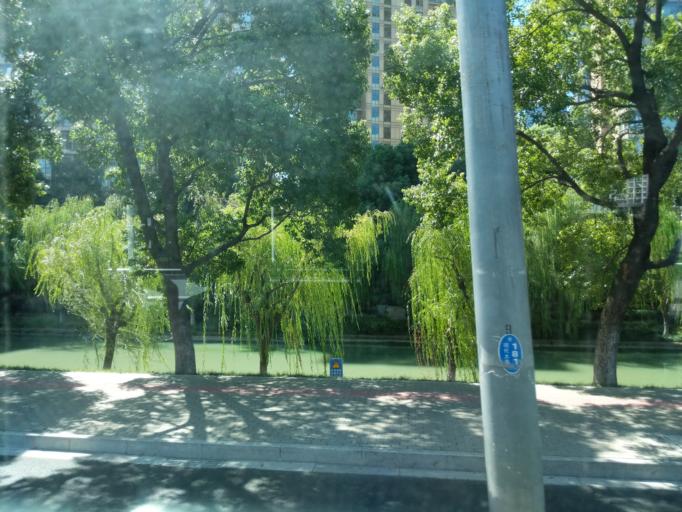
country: CN
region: Jiangsu Sheng
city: Weiting
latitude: 31.3247
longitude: 120.6751
